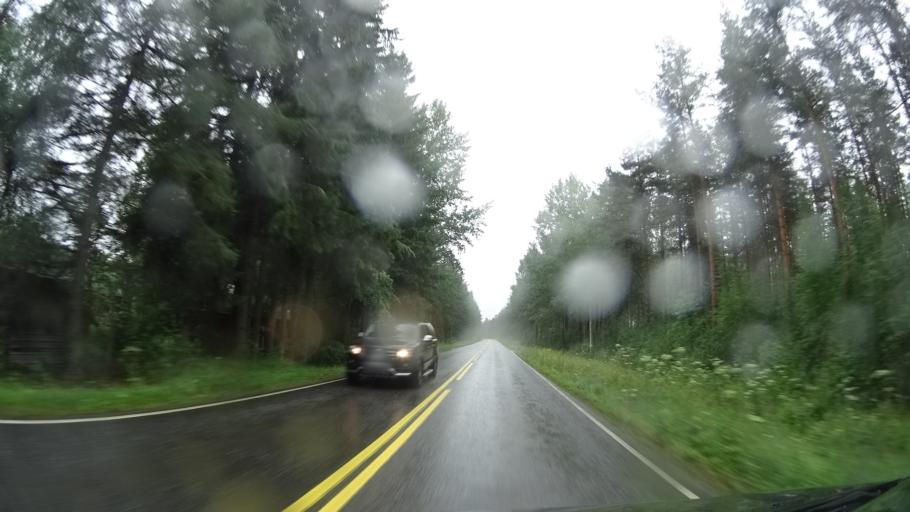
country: FI
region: North Karelia
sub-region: Keski-Karjala
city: Raeaekkylae
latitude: 62.3049
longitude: 29.5604
